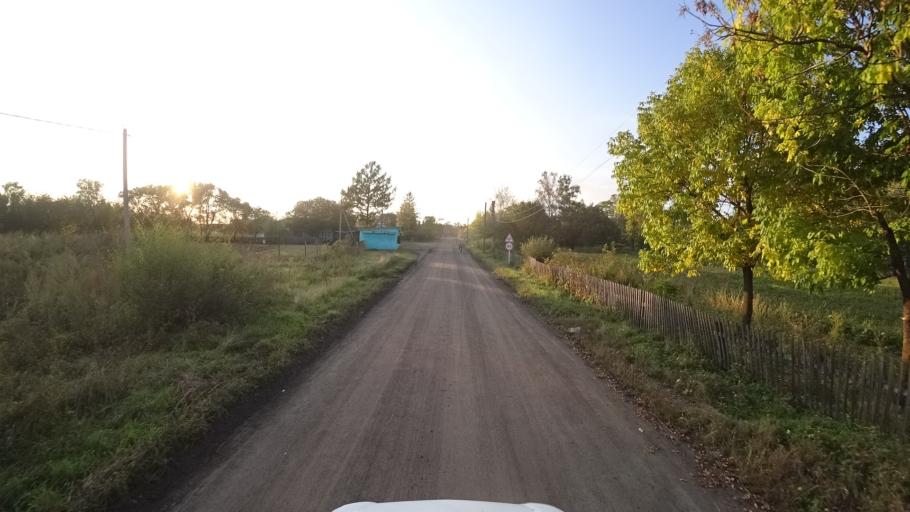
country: RU
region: Amur
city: Arkhara
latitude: 49.3596
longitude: 130.1171
